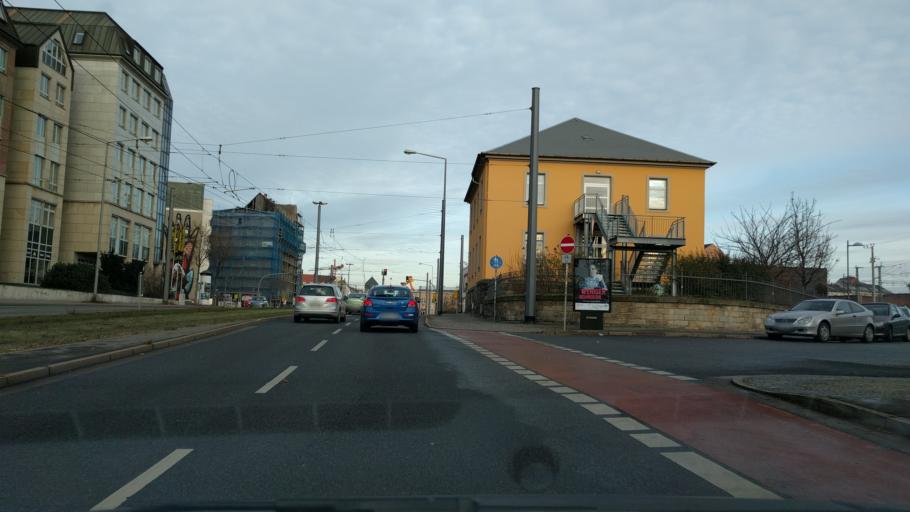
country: DE
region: Saxony
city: Dresden
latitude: 51.0533
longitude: 13.7181
